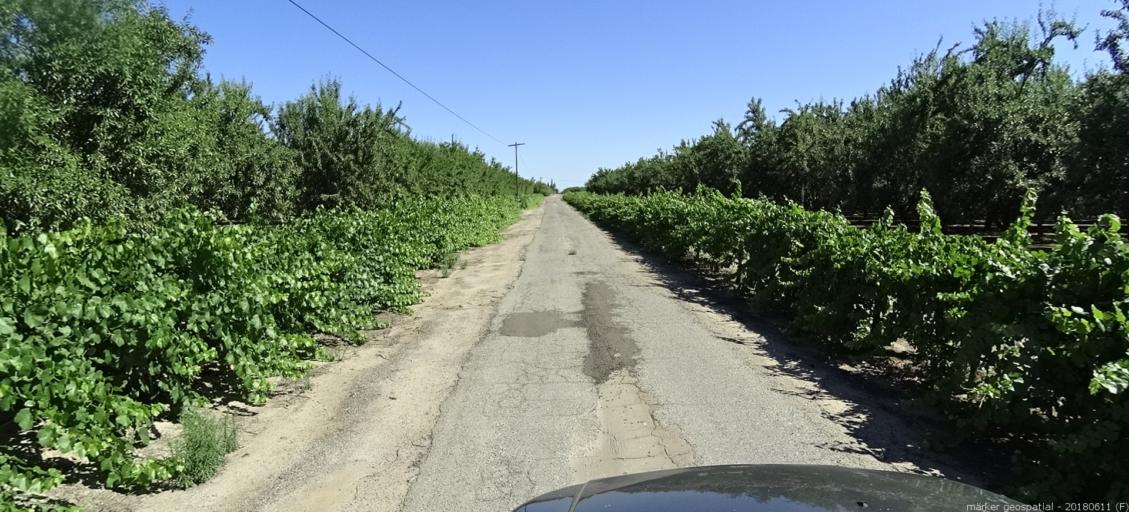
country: US
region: California
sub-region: Madera County
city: Madera
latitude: 36.9508
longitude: -120.1749
